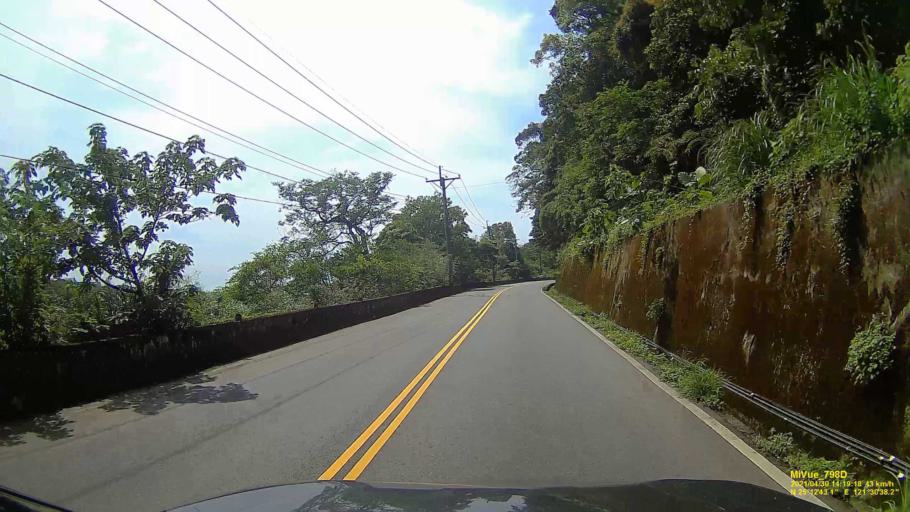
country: TW
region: Taipei
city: Taipei
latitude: 25.2119
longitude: 121.5106
